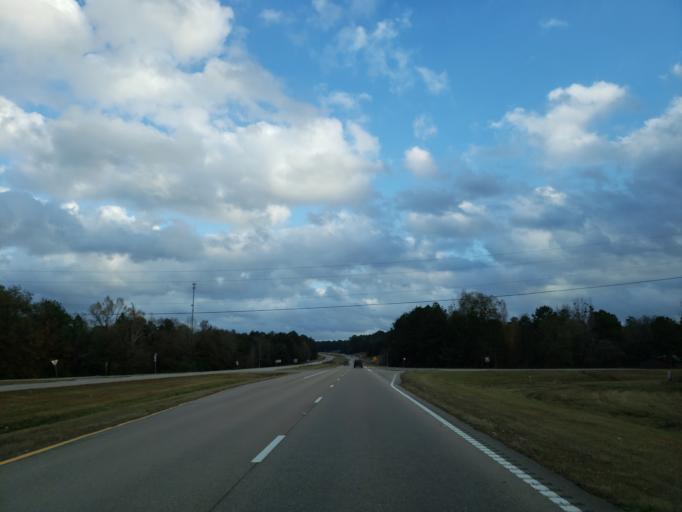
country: US
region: Mississippi
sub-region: Perry County
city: New Augusta
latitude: 31.1598
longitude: -88.9237
